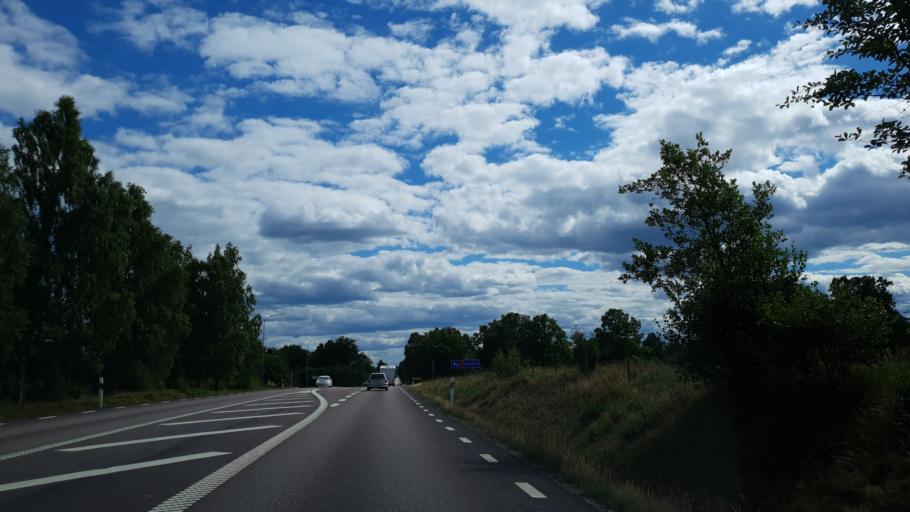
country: SE
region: Kronoberg
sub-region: Lessebo Kommun
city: Lessebo
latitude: 56.8591
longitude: 15.3879
